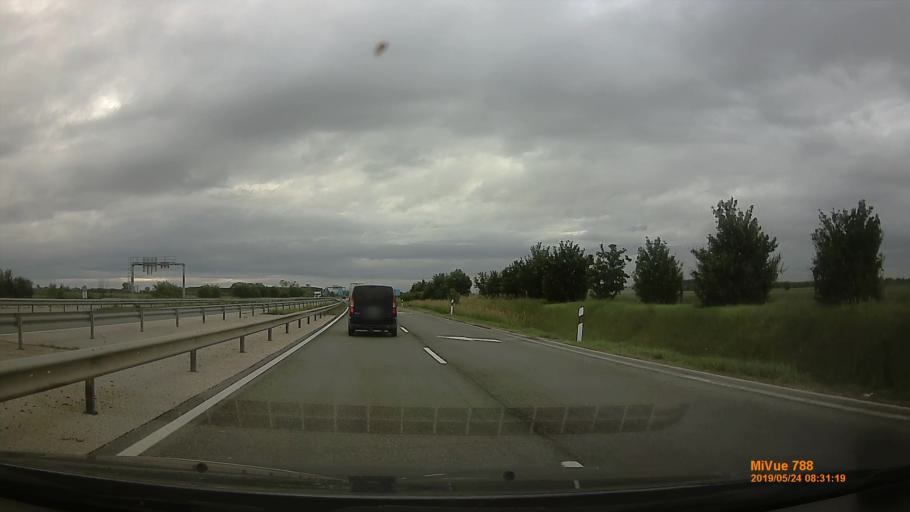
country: HU
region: Pest
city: Vecses
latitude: 47.4039
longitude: 19.3220
